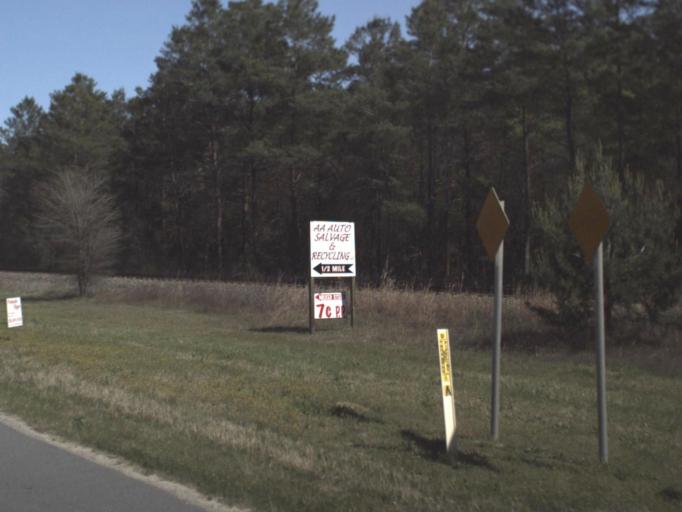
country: US
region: Florida
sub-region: Walton County
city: DeFuniak Springs
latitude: 30.7433
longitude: -86.3138
